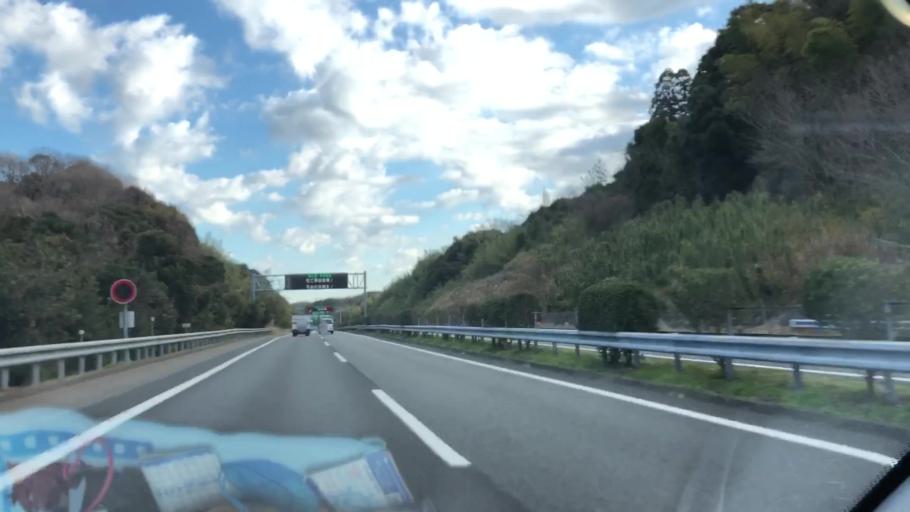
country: JP
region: Chiba
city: Kisarazu
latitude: 35.3682
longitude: 139.9660
